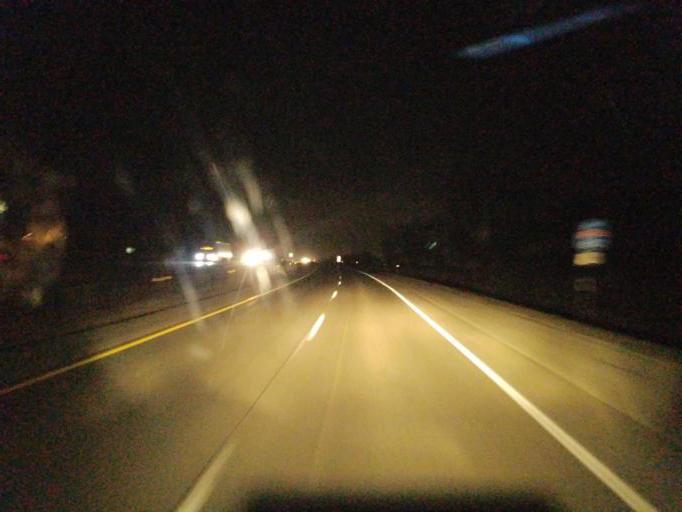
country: US
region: Iowa
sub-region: Dallas County
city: De Soto
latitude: 41.5216
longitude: -94.0669
